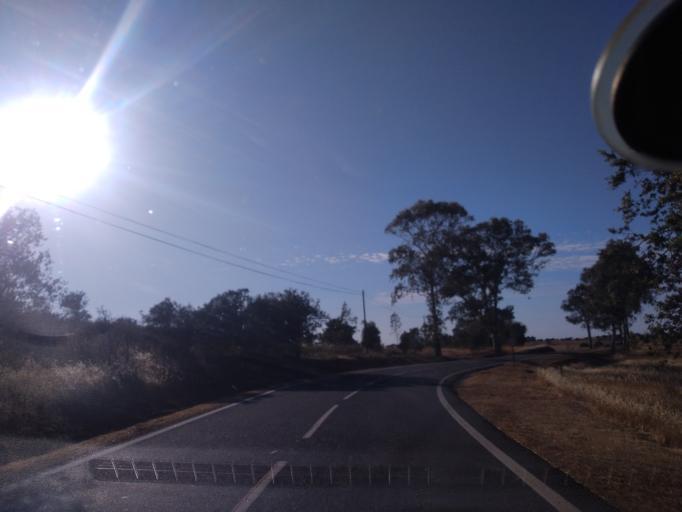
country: PT
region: Beja
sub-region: Almodovar
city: Almodovar
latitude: 37.4398
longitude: -7.9873
